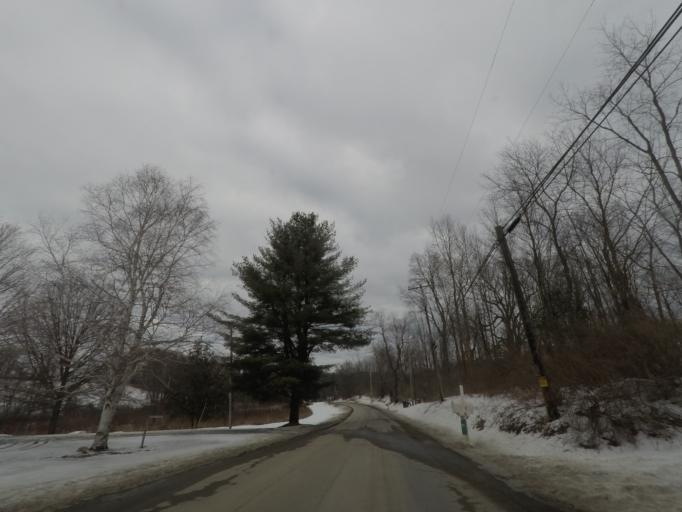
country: US
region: New York
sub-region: Rensselaer County
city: Poestenkill
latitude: 42.7345
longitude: -73.5732
